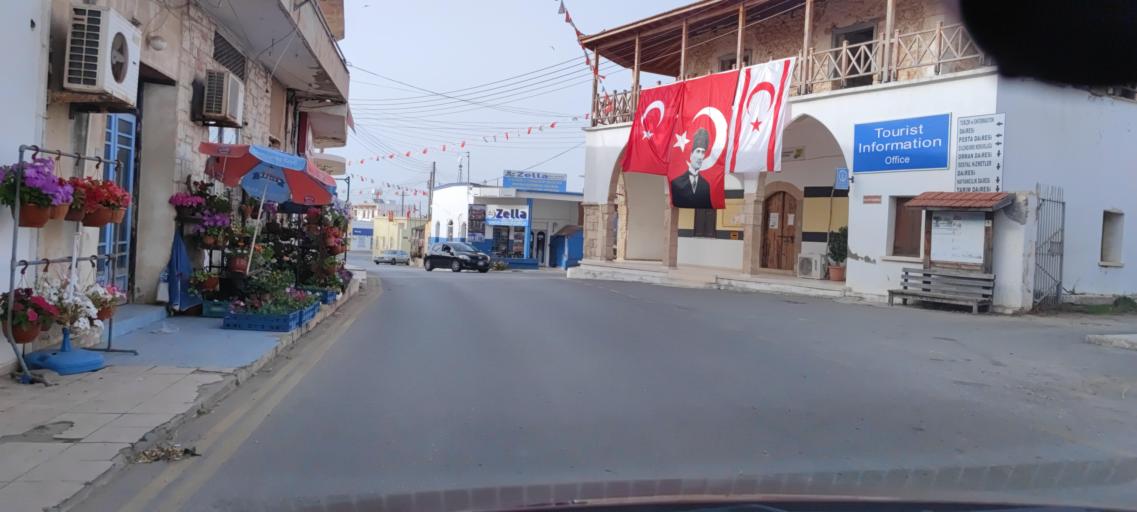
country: CY
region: Ammochostos
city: Leonarisso
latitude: 35.5346
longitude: 34.1887
